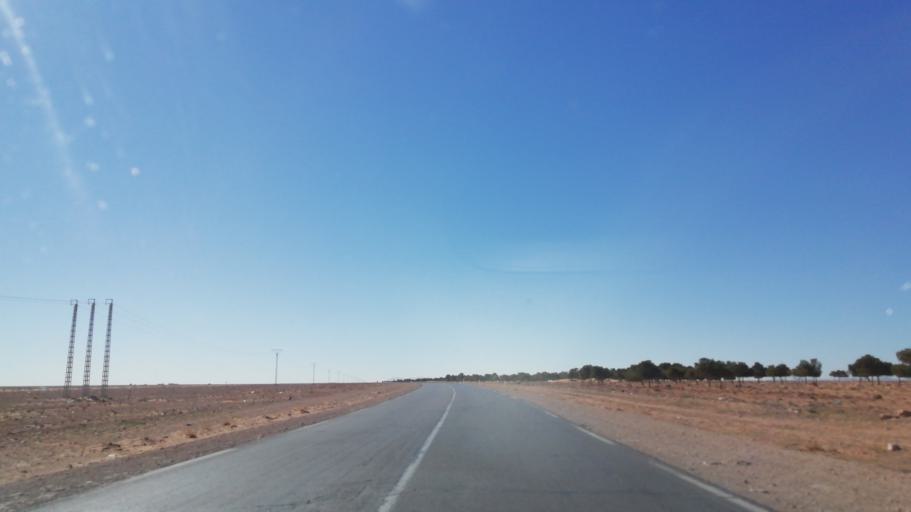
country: DZ
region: Saida
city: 'Ain el Hadjar
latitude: 34.0021
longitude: 0.0446
